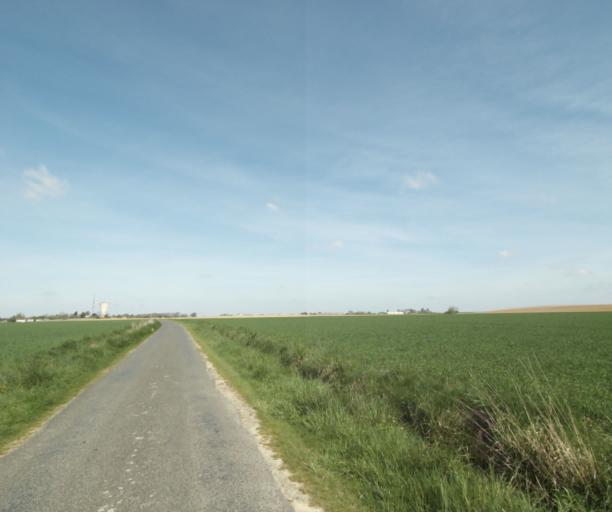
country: FR
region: Ile-de-France
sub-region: Departement de Seine-et-Marne
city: Nangis
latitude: 48.5480
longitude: 3.0346
